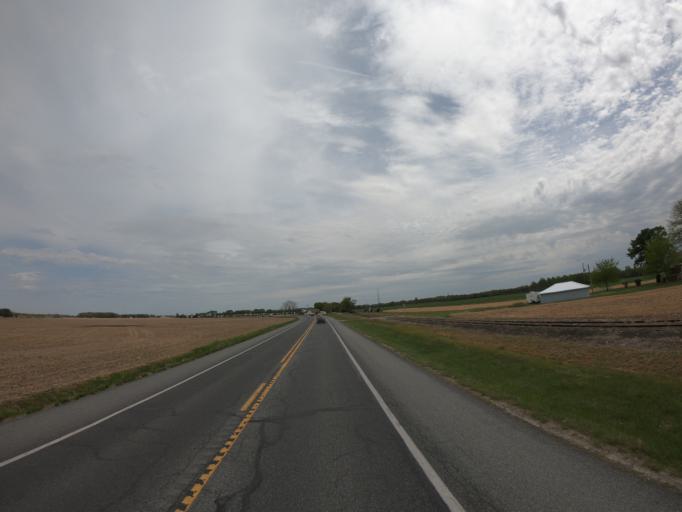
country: US
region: Delaware
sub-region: Sussex County
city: Milton
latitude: 38.7858
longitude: -75.3606
